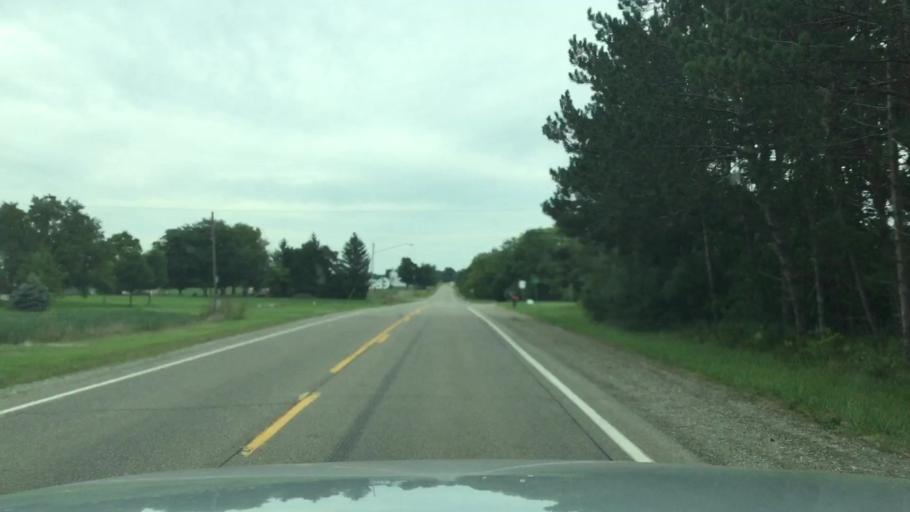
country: US
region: Michigan
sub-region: Genesee County
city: Swartz Creek
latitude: 42.9568
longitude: -83.9125
